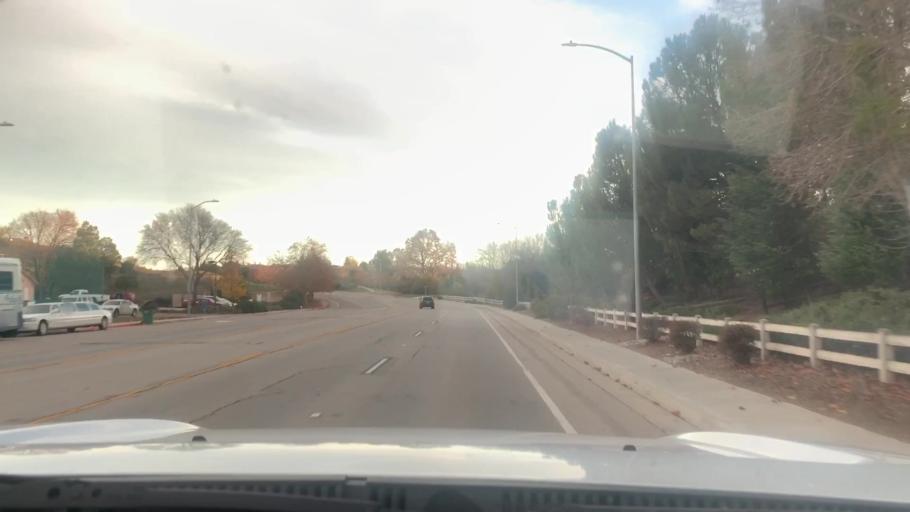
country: US
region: California
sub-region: San Luis Obispo County
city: Paso Robles
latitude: 35.6358
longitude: -120.6582
